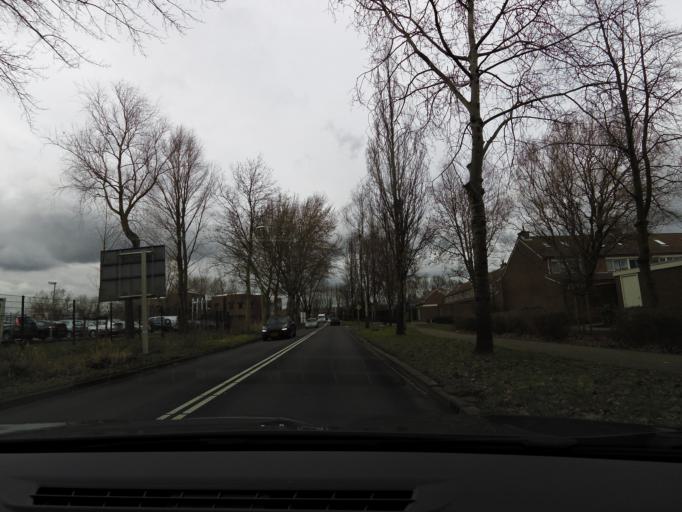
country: NL
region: South Holland
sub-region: Gemeente Gouda
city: Gouda
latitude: 52.0271
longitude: 4.7164
